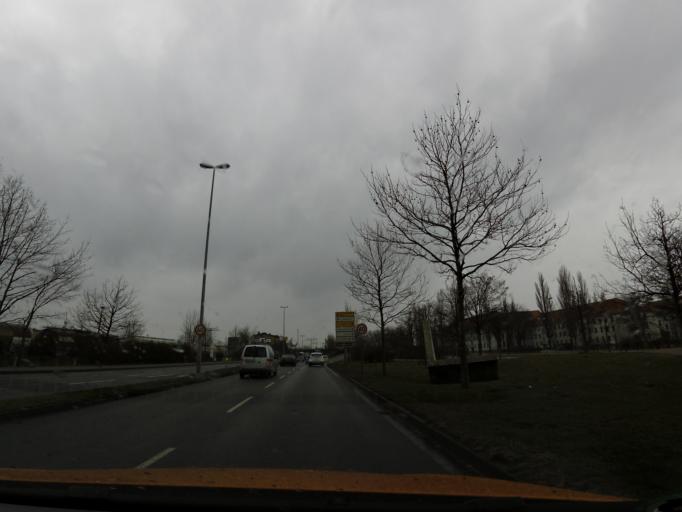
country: DE
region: Brandenburg
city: Brandenburg an der Havel
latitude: 52.4105
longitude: 12.5328
